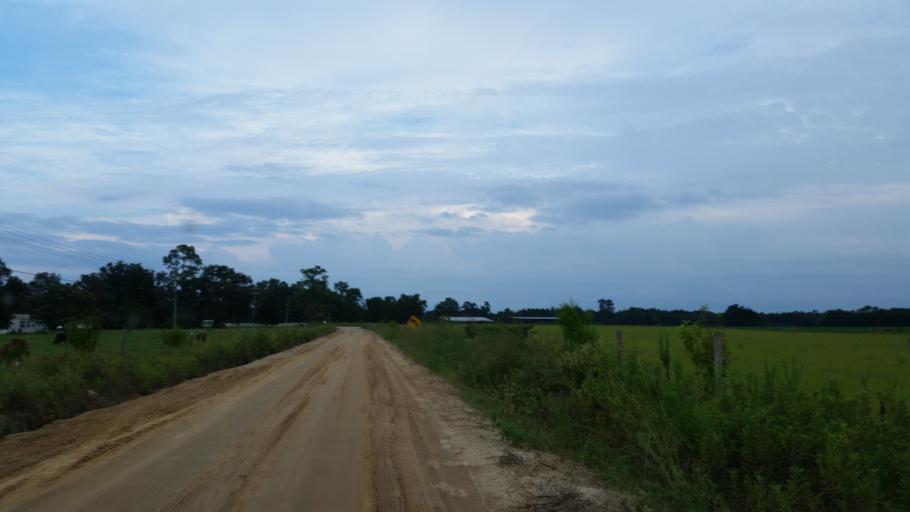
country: US
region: Georgia
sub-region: Lowndes County
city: Valdosta
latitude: 30.7233
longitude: -83.3174
